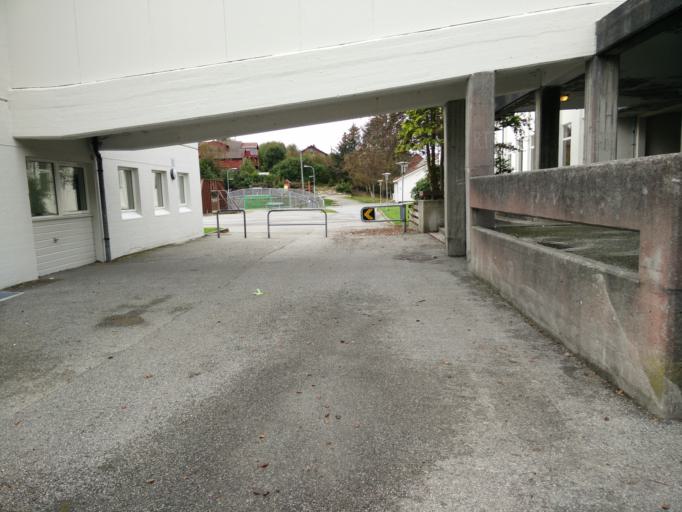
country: NO
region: Hordaland
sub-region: Sveio
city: Sveio
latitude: 59.6007
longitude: 5.2105
